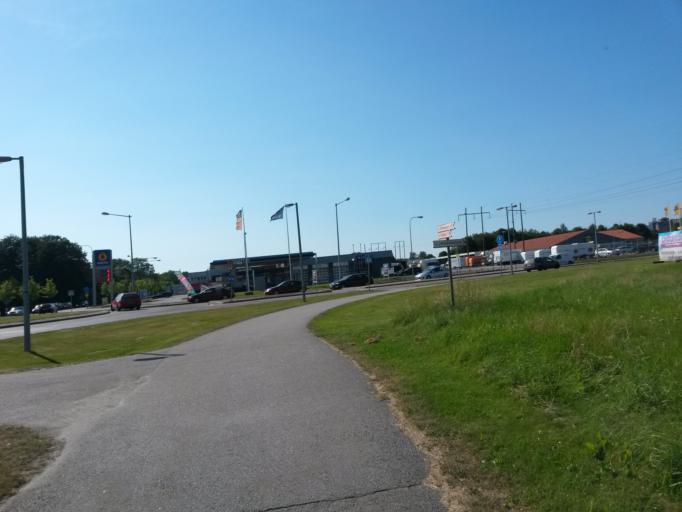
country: SE
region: Vaestra Goetaland
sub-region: Lidkopings Kommun
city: Lidkoping
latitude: 58.4968
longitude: 13.1820
